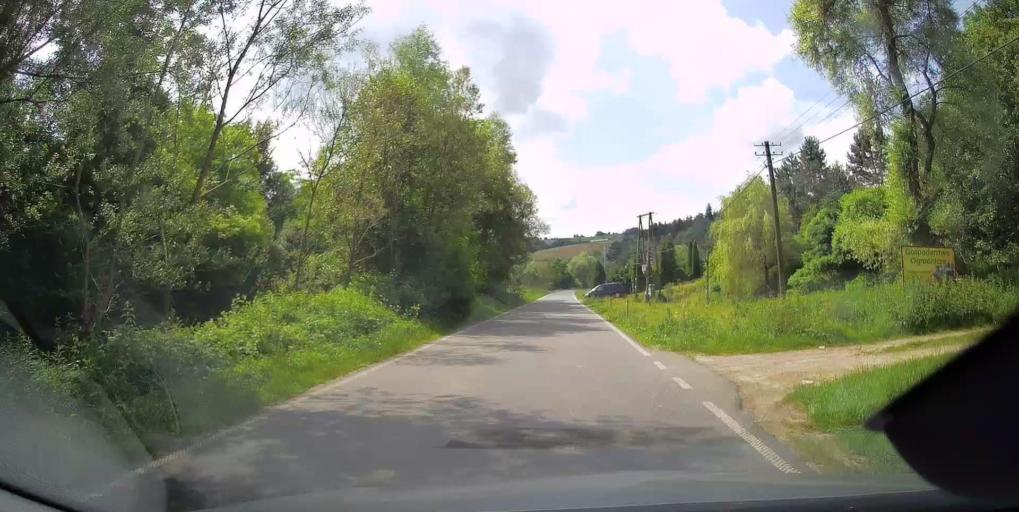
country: PL
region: Lesser Poland Voivodeship
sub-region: Powiat nowosadecki
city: Korzenna
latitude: 49.7449
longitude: 20.7694
